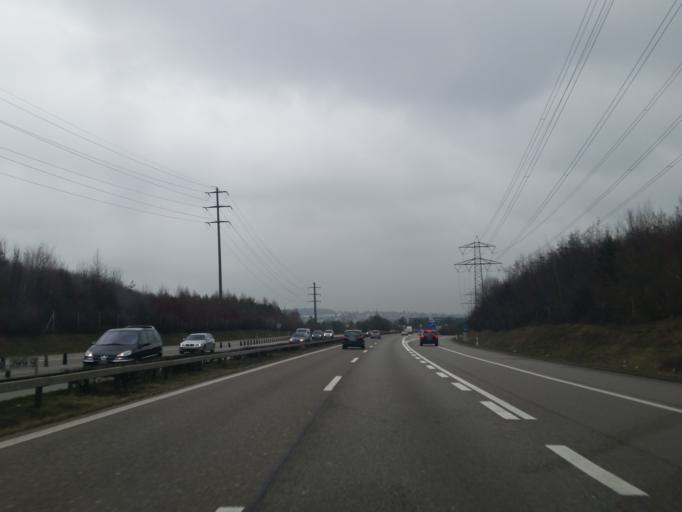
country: CH
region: Zurich
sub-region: Bezirk Zuerich
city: Zuerich (Kreis 11) / Seebach
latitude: 47.4323
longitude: 8.5442
